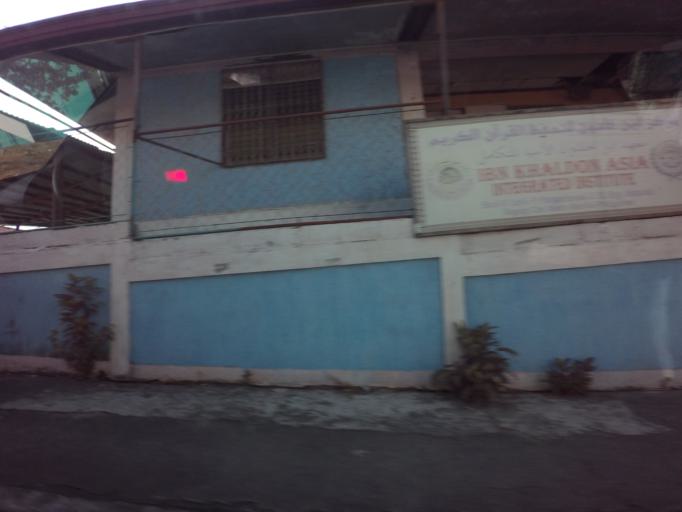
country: PH
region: Calabarzon
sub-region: Province of Rizal
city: Taguig
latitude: 14.4982
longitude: 121.0528
